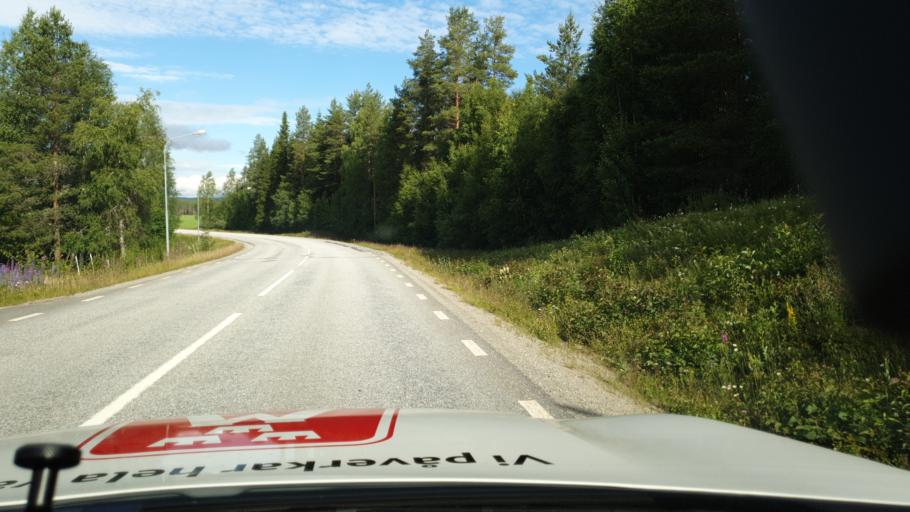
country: SE
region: Vaesterbotten
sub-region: Vindelns Kommun
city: Vindeln
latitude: 64.1121
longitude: 19.5825
